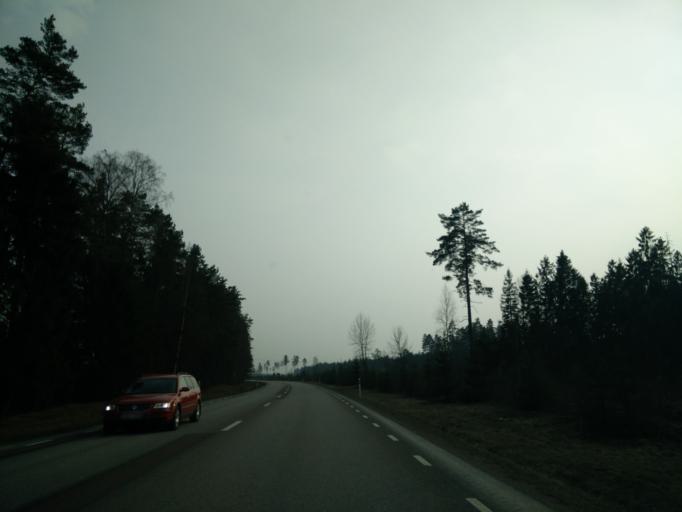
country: SE
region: Vaermland
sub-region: Forshaga Kommun
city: Forshaga
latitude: 59.5097
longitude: 13.4378
